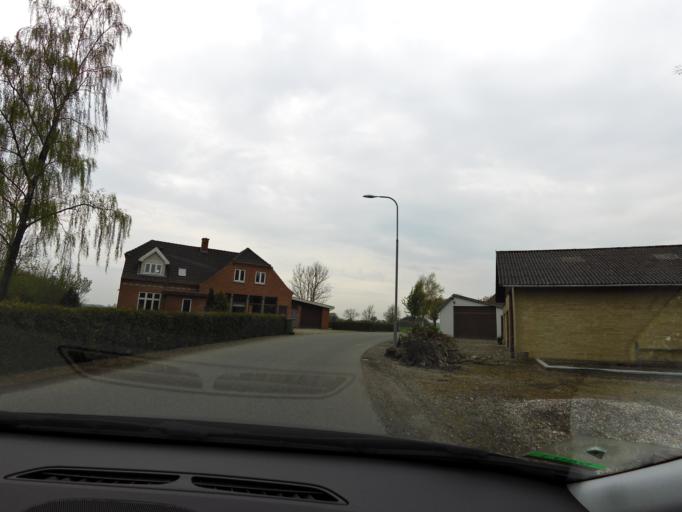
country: DK
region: South Denmark
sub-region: Faaborg-Midtfyn Kommune
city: Ringe
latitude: 55.1909
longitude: 10.5420
